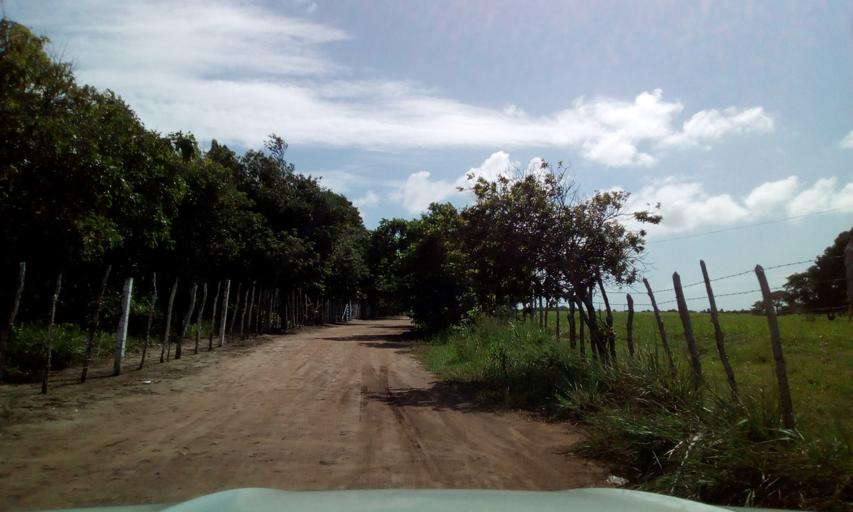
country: BR
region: Paraiba
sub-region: Conde
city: Conde
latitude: -7.2243
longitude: -34.8211
